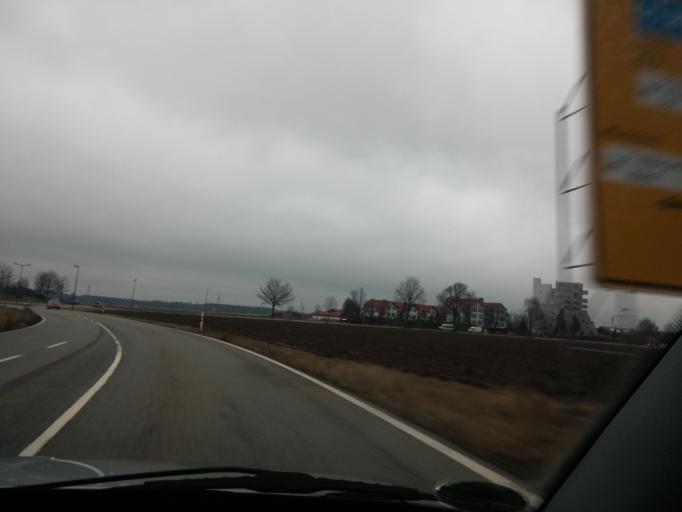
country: DE
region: Bavaria
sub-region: Upper Bavaria
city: Putzbrunn
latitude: 48.0769
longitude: 11.7073
